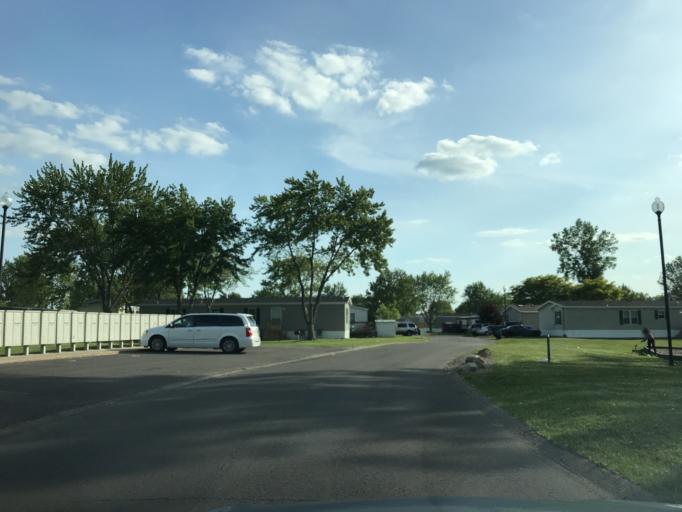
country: US
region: Michigan
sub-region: Oakland County
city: Walled Lake
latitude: 42.5163
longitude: -83.4590
